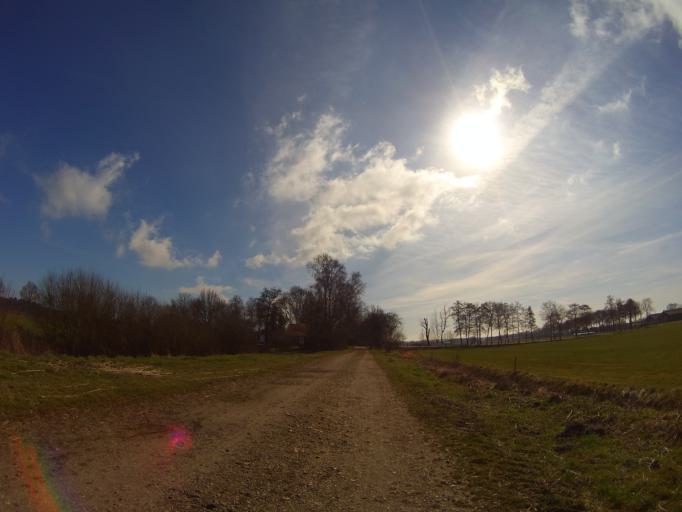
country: NL
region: Utrecht
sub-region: Gemeente Woudenberg
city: Woudenberg
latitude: 52.0744
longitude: 5.4557
